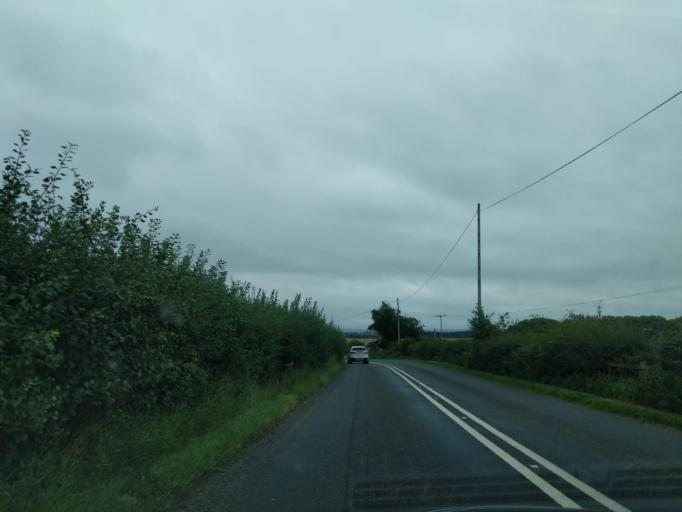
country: GB
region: Scotland
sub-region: East Lothian
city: Ormiston
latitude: 55.9077
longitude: -2.9179
